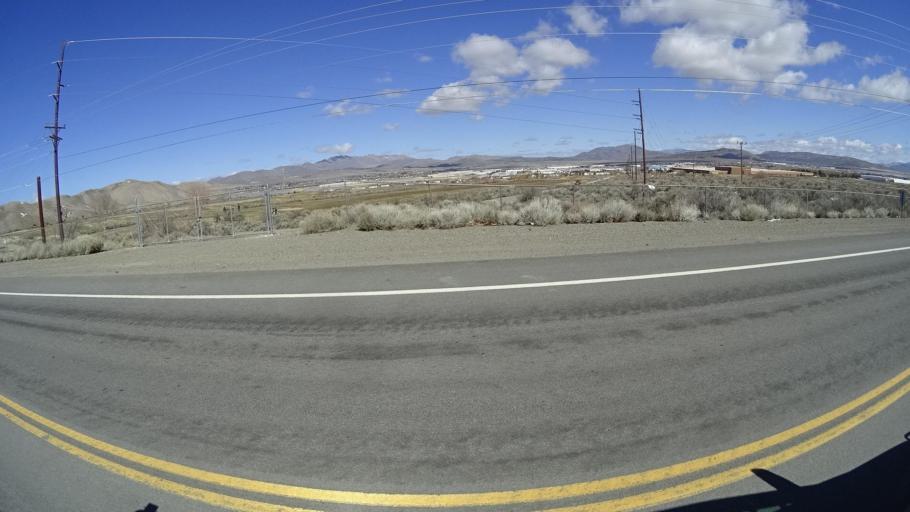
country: US
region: Nevada
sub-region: Washoe County
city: Lemmon Valley
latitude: 39.6256
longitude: -119.8938
